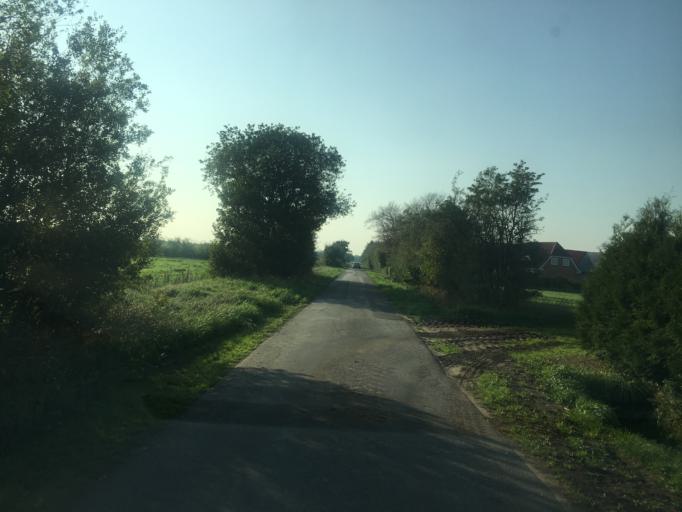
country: DE
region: Schleswig-Holstein
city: Ladelund
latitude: 54.9244
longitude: 9.0240
